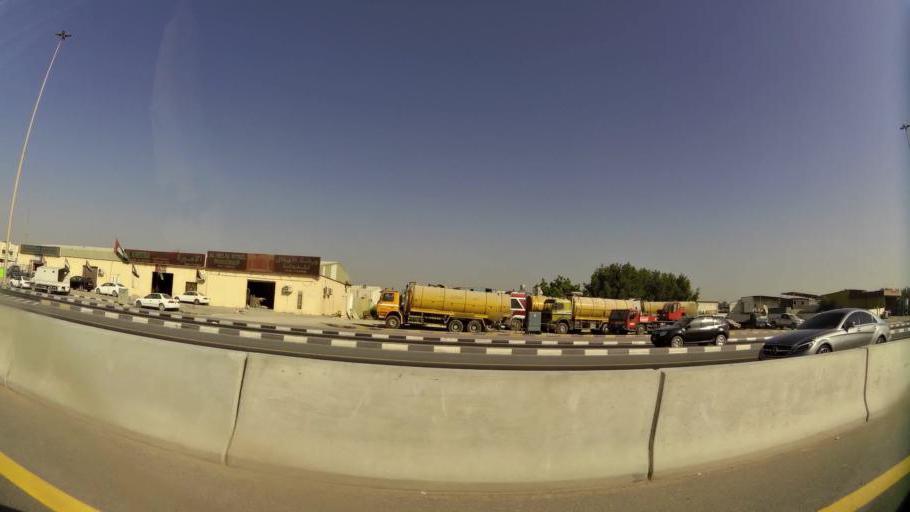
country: AE
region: Ash Shariqah
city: Sharjah
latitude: 25.3251
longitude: 55.4178
